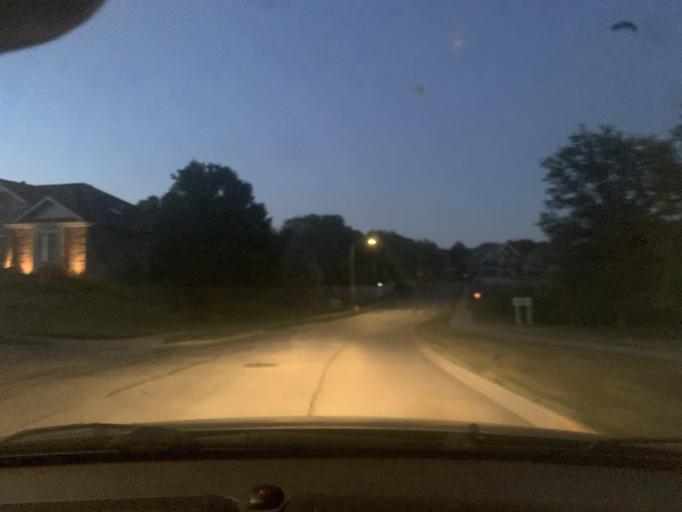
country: US
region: Nebraska
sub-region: Sarpy County
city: La Vista
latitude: 41.1794
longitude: -96.0558
